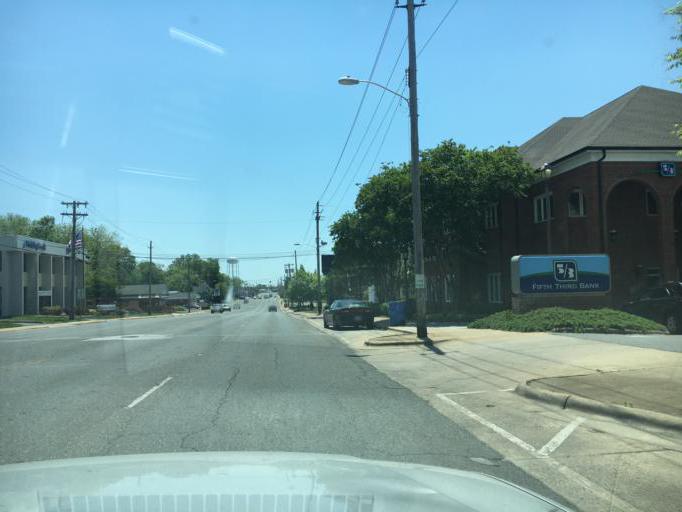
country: US
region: North Carolina
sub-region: Cleveland County
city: Shelby
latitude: 35.2890
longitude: -81.5405
